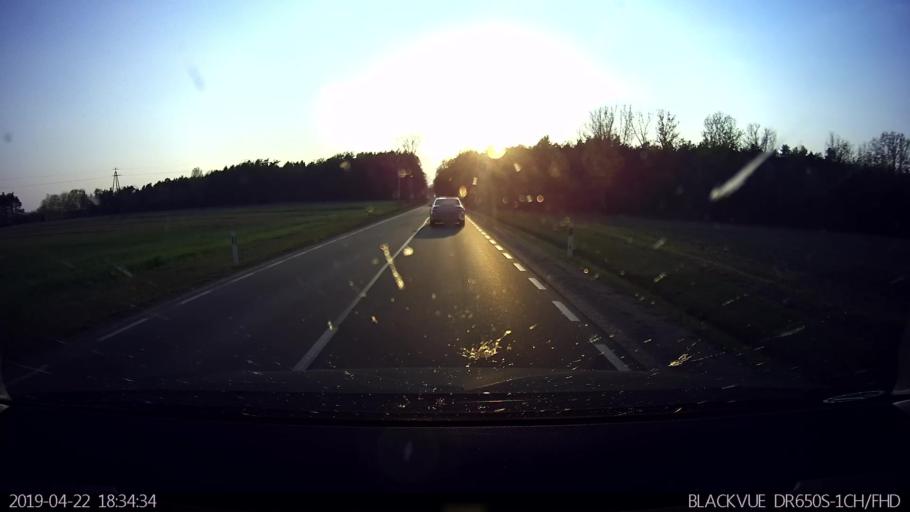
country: PL
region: Masovian Voivodeship
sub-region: Powiat wolominski
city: Klembow
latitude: 52.4454
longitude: 21.3663
